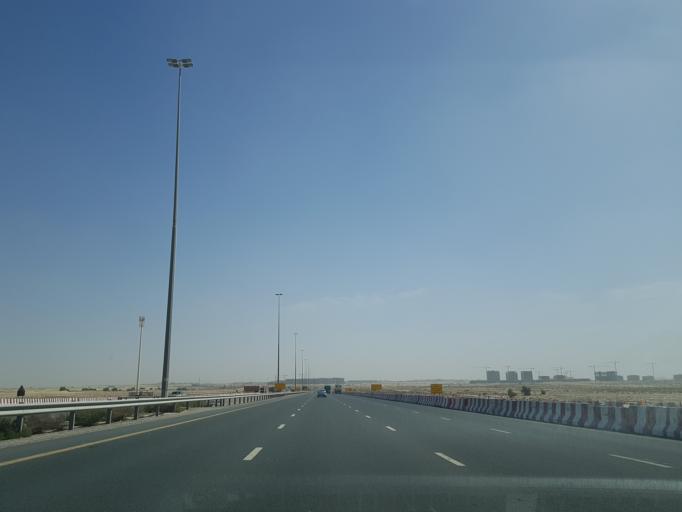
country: AE
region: Dubai
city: Dubai
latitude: 24.9588
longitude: 55.2068
